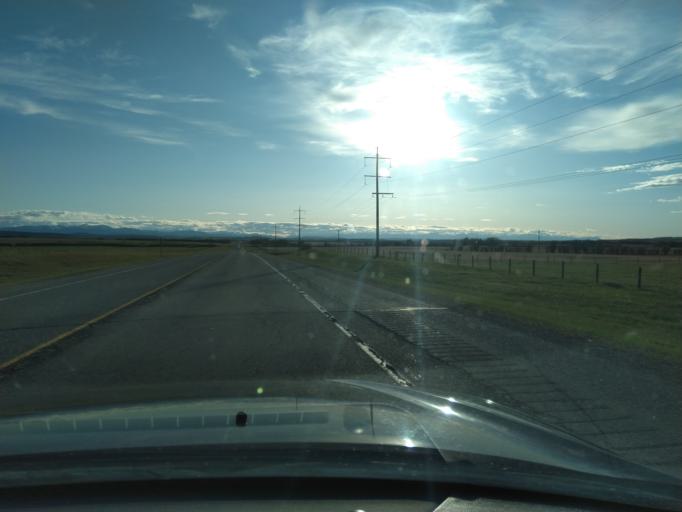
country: CA
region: Alberta
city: Cochrane
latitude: 51.0235
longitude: -114.3376
